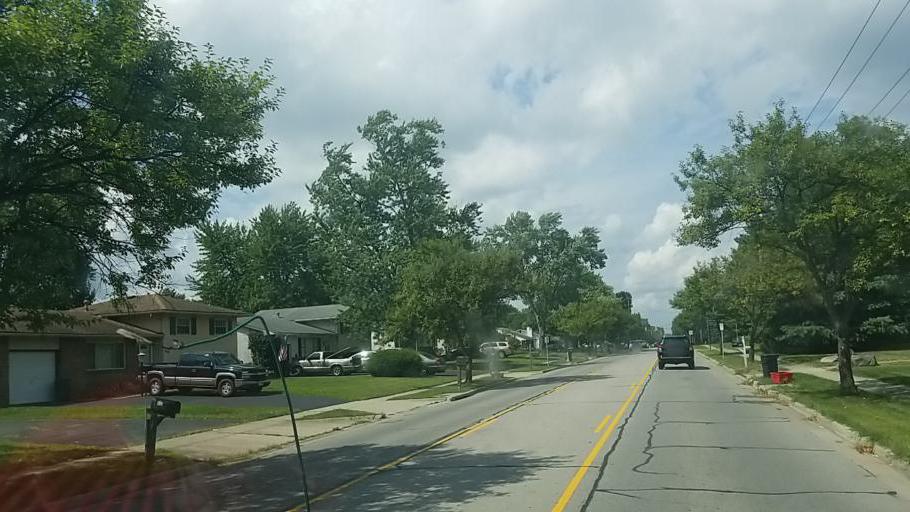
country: US
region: Ohio
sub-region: Franklin County
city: Gahanna
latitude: 40.0306
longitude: -82.8896
